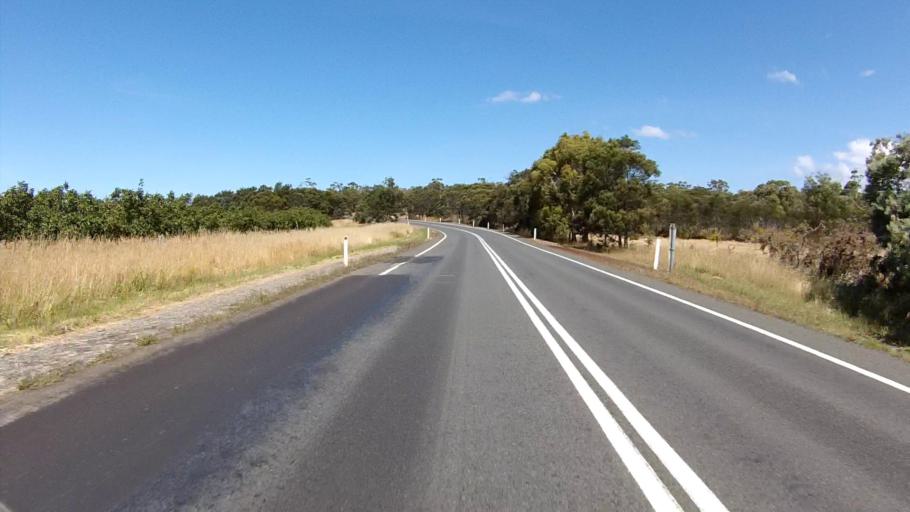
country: AU
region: Tasmania
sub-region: Break O'Day
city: St Helens
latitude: -42.0756
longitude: 148.0672
